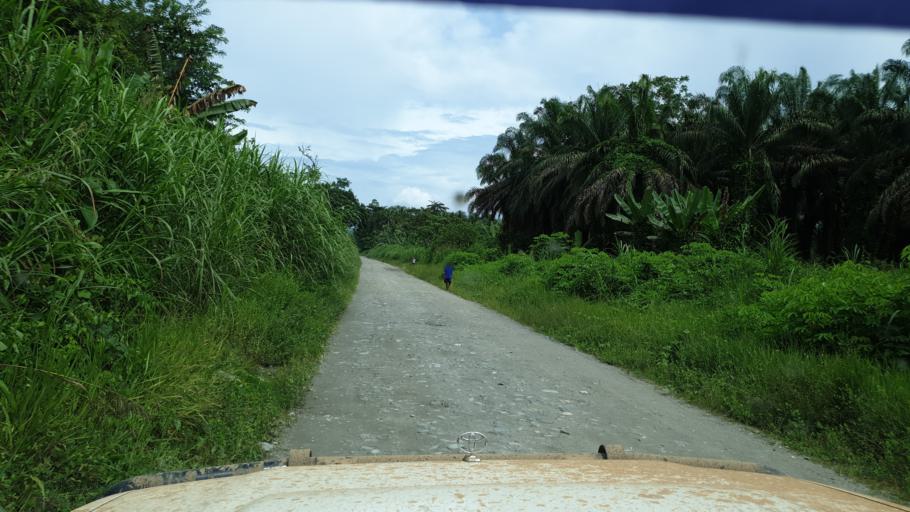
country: PG
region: Northern Province
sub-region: Sohe
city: Kokoda
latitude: -8.8962
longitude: 147.7507
